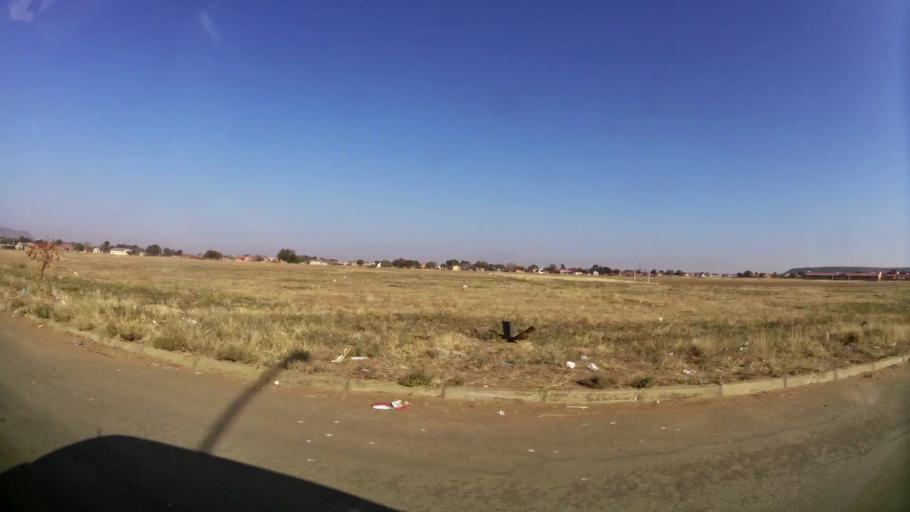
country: ZA
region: Orange Free State
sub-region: Mangaung Metropolitan Municipality
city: Bloemfontein
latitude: -29.1825
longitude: 26.1797
